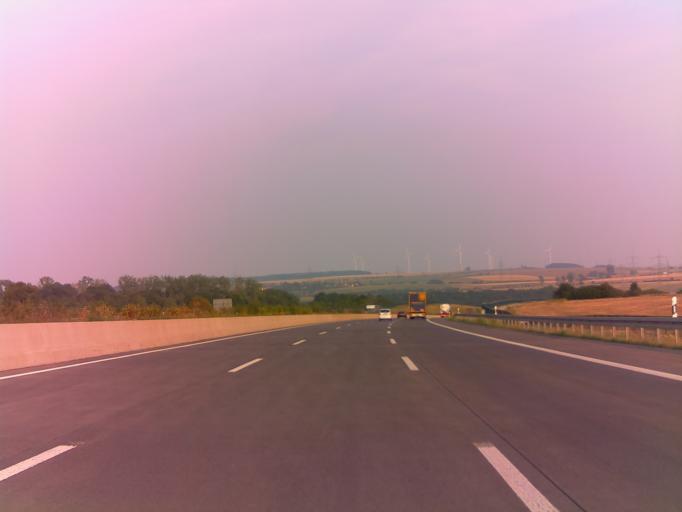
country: DE
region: Thuringia
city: Haina
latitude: 50.9869
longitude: 10.4702
